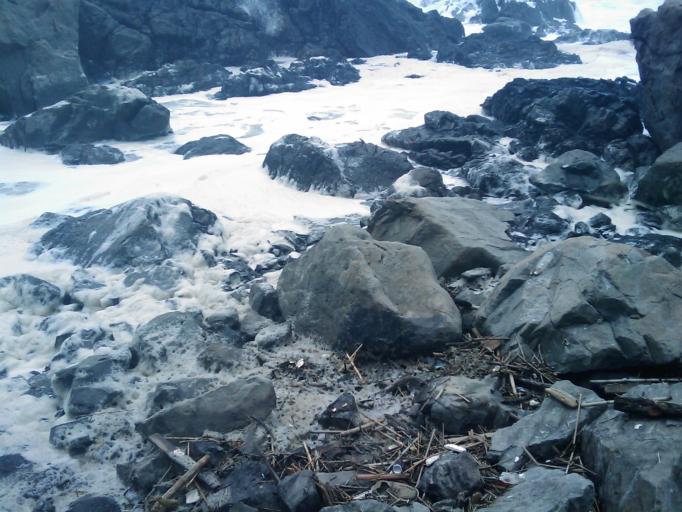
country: JP
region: Wakayama
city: Gobo
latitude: 33.8802
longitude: 135.0583
